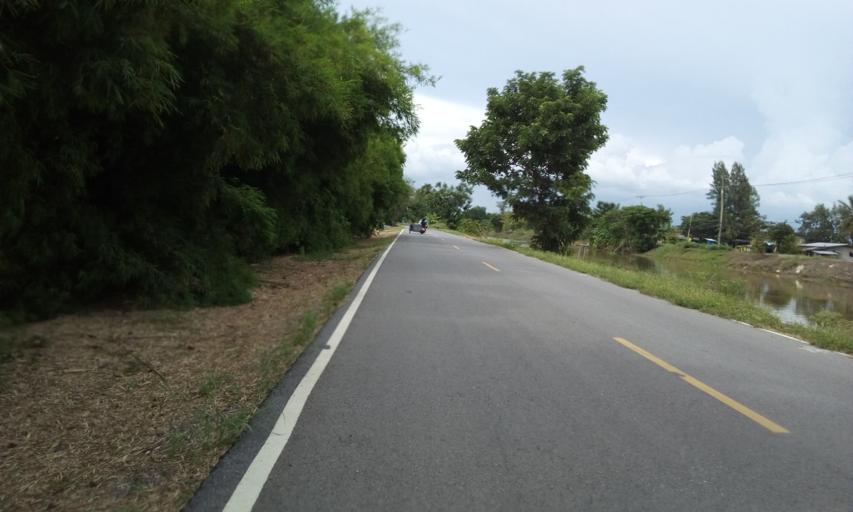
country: TH
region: Pathum Thani
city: Nong Suea
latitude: 14.1767
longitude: 100.8231
